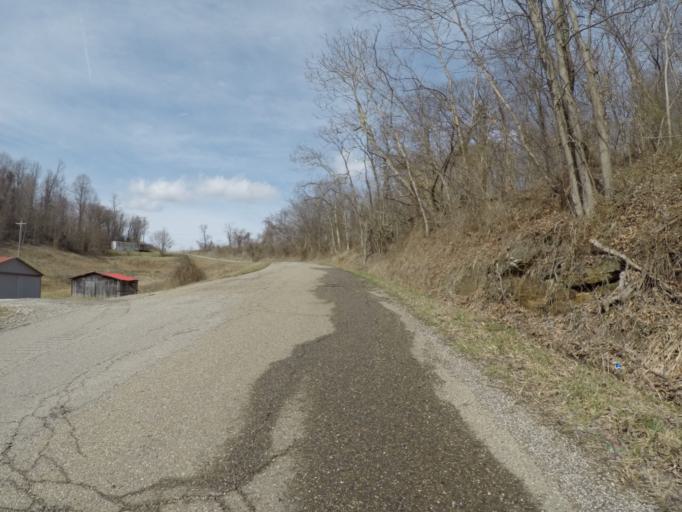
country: US
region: Ohio
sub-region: Lawrence County
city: Burlington
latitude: 38.4849
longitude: -82.5367
